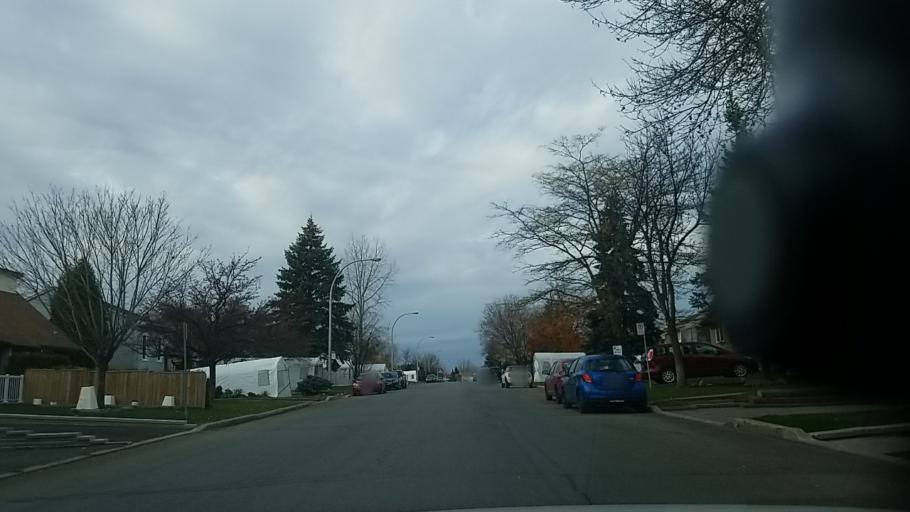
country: CA
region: Quebec
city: Dollard-Des Ormeaux
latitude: 45.5365
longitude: -73.7849
